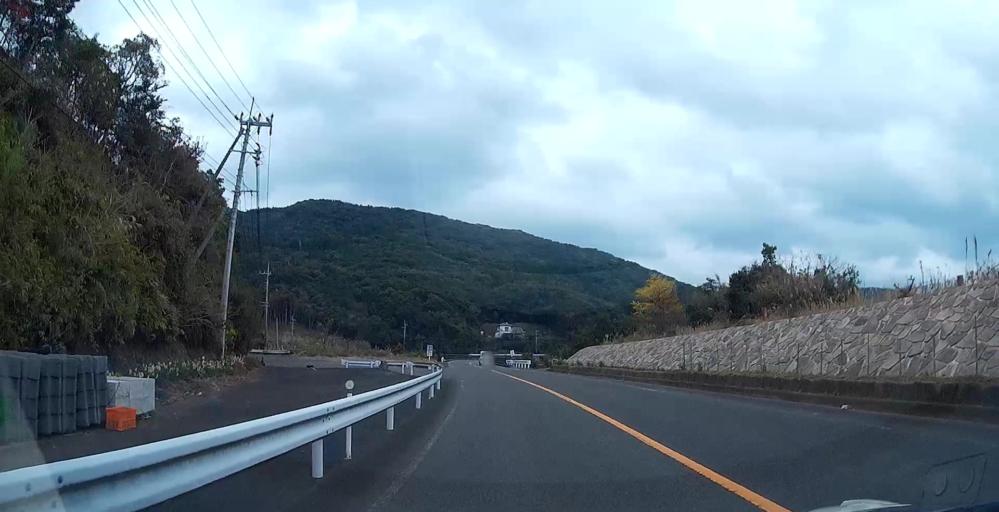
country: JP
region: Kagoshima
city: Akune
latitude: 32.1052
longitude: 130.1495
